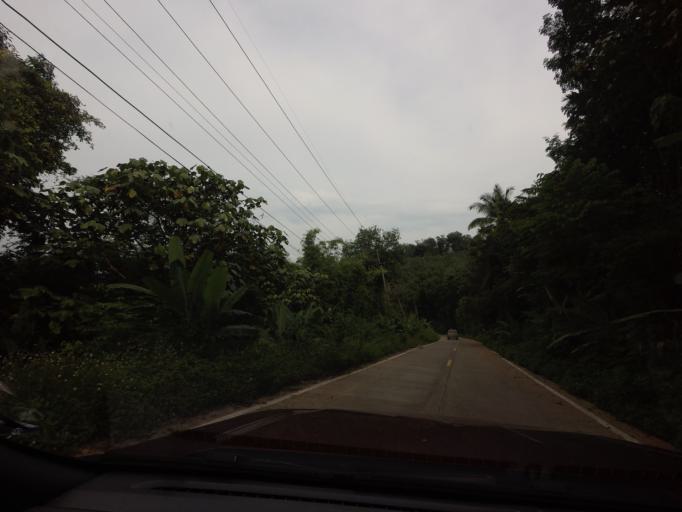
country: TH
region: Yala
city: Than To
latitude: 6.0699
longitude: 101.3527
